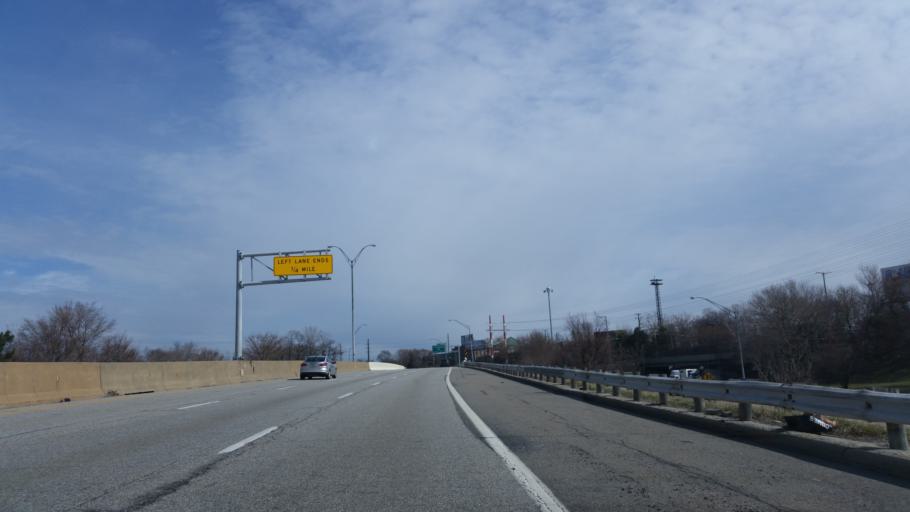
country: US
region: Ohio
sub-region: Cuyahoga County
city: Cleveland
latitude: 41.5164
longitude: -81.6773
